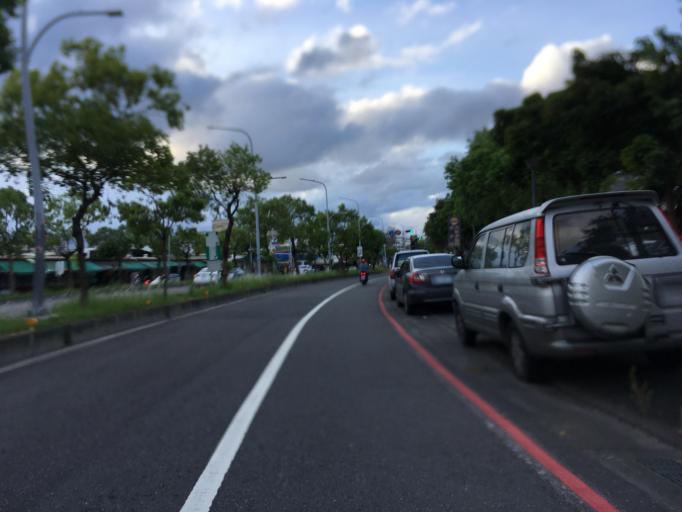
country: TW
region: Taiwan
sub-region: Yilan
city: Yilan
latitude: 24.6709
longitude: 121.7643
